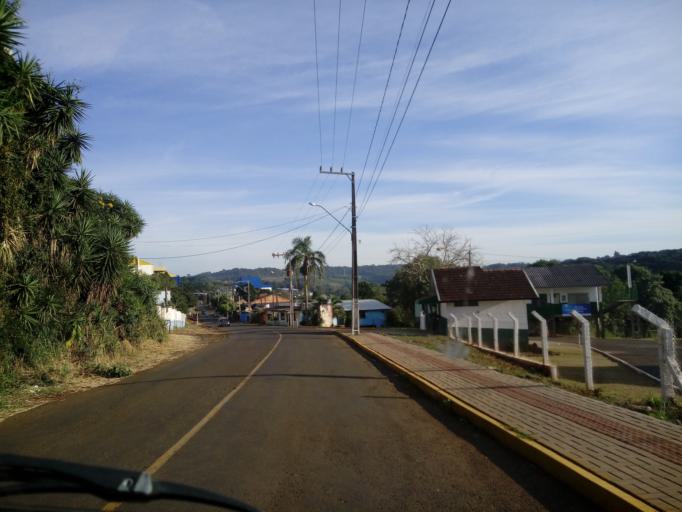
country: BR
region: Santa Catarina
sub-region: Chapeco
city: Chapeco
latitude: -27.0936
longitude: -52.6629
